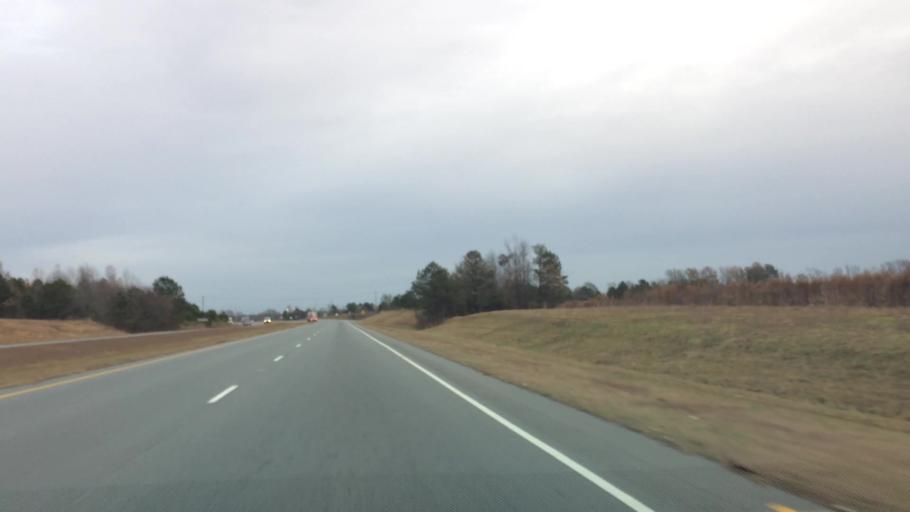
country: US
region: North Carolina
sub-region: Wayne County
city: Mount Olive
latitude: 35.1265
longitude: -78.1574
